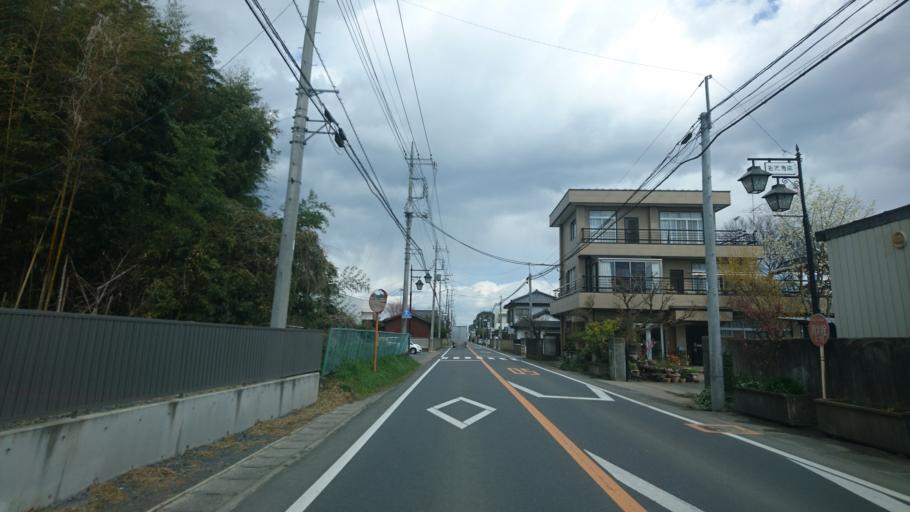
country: JP
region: Ibaraki
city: Yuki
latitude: 36.2298
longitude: 139.9319
